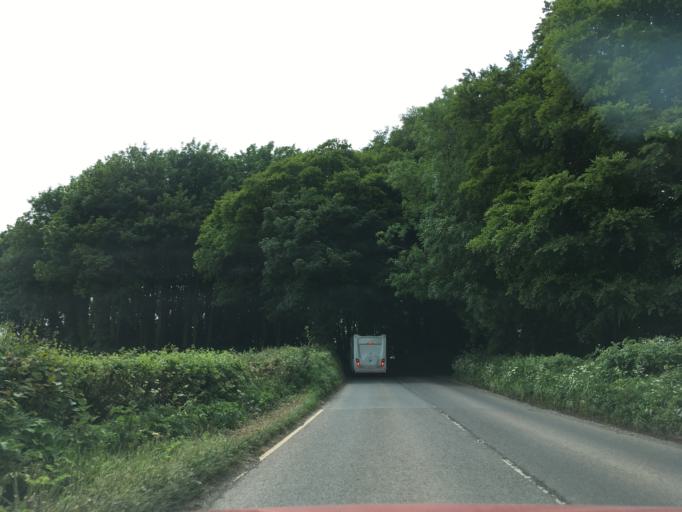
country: GB
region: England
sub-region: Devon
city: Totnes
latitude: 50.4194
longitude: -3.7041
